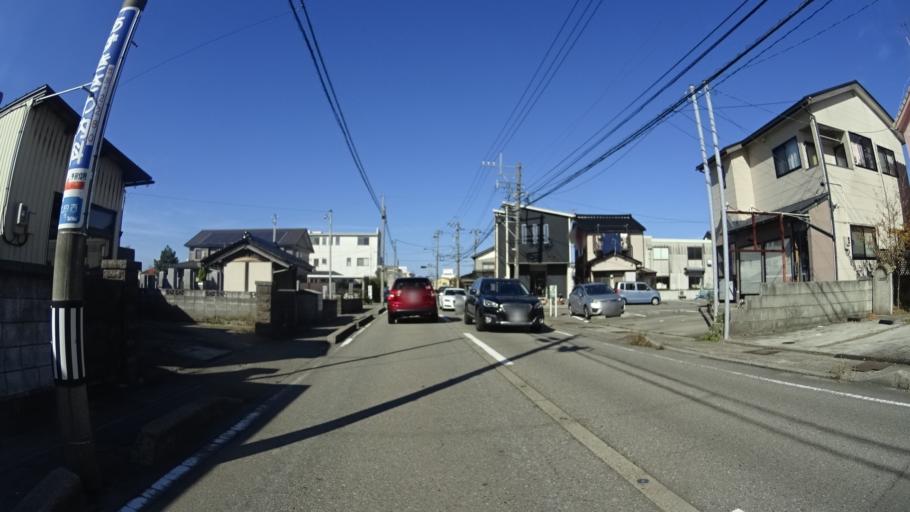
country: JP
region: Ishikawa
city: Kanazawa-shi
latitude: 36.5962
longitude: 136.6093
